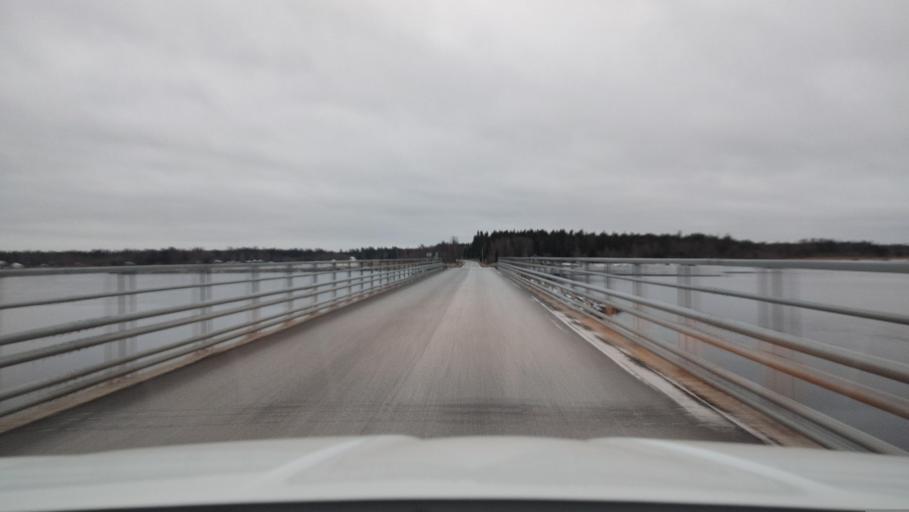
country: FI
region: Ostrobothnia
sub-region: Vaasa
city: Replot
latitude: 63.2746
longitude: 21.3438
